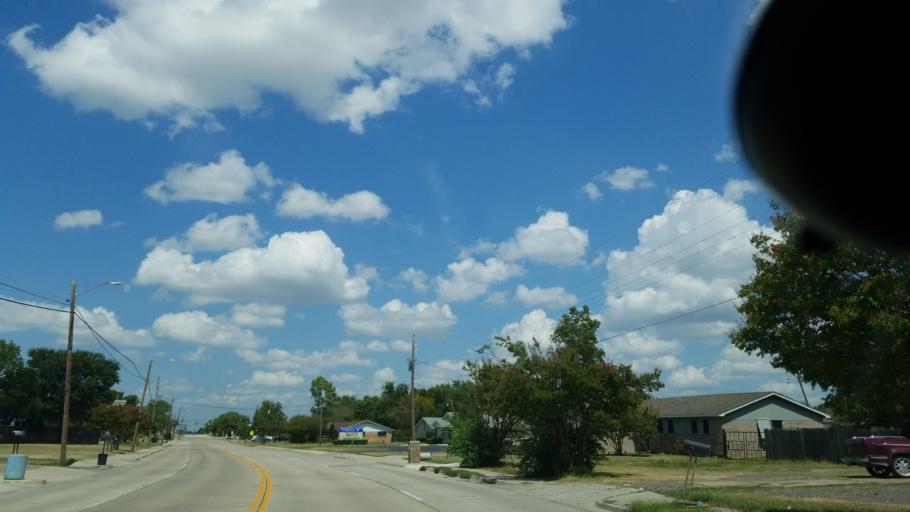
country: US
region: Texas
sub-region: Dallas County
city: Grand Prairie
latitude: 32.7175
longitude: -96.9859
